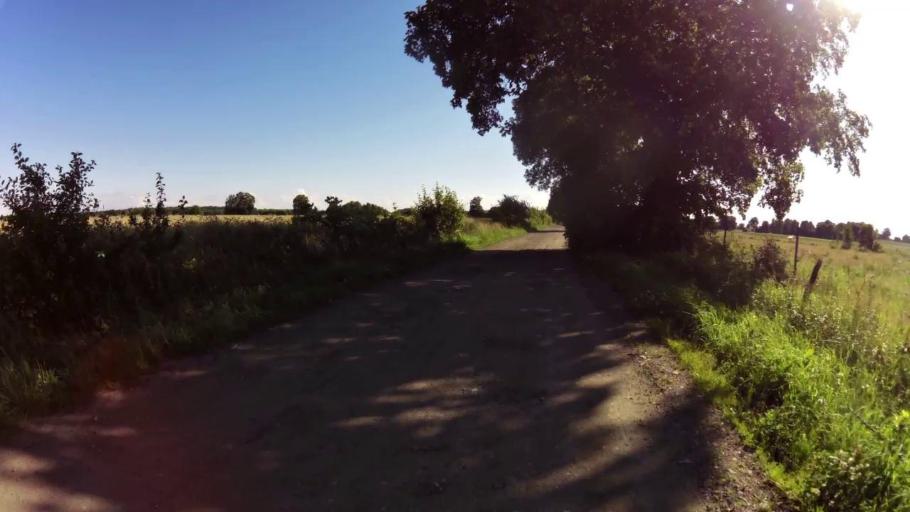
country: PL
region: West Pomeranian Voivodeship
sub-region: Powiat bialogardzki
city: Bialogard
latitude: 54.0169
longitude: 16.0781
